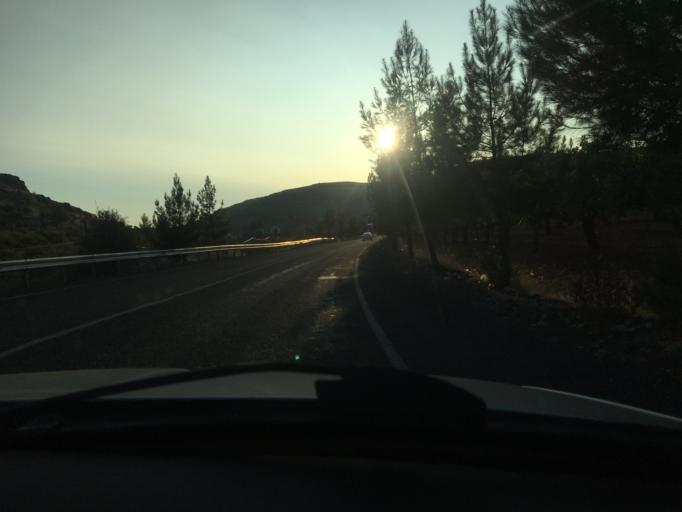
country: TR
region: Sanliurfa
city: Halfeti
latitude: 37.2226
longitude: 37.9583
